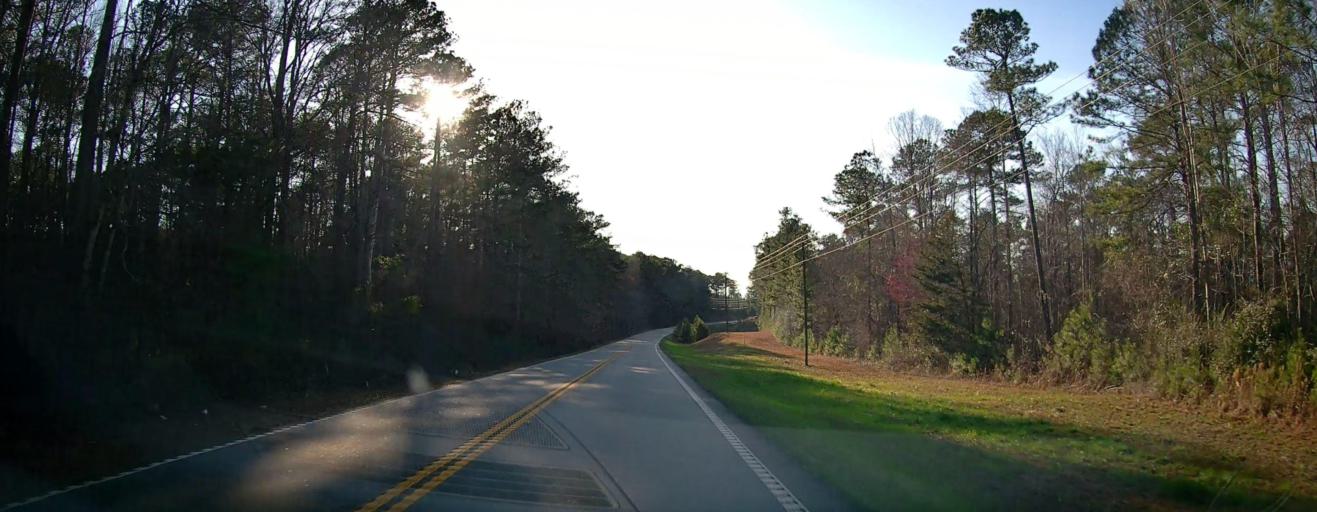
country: US
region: Alabama
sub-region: Chambers County
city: Valley
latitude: 32.7427
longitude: -85.0418
